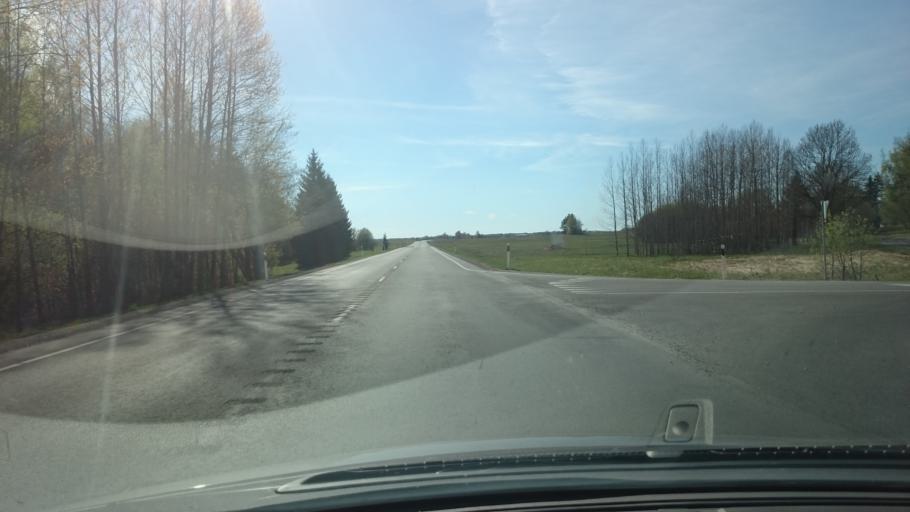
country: EE
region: Laeaene-Virumaa
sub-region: Haljala vald
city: Haljala
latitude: 59.3486
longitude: 26.2659
